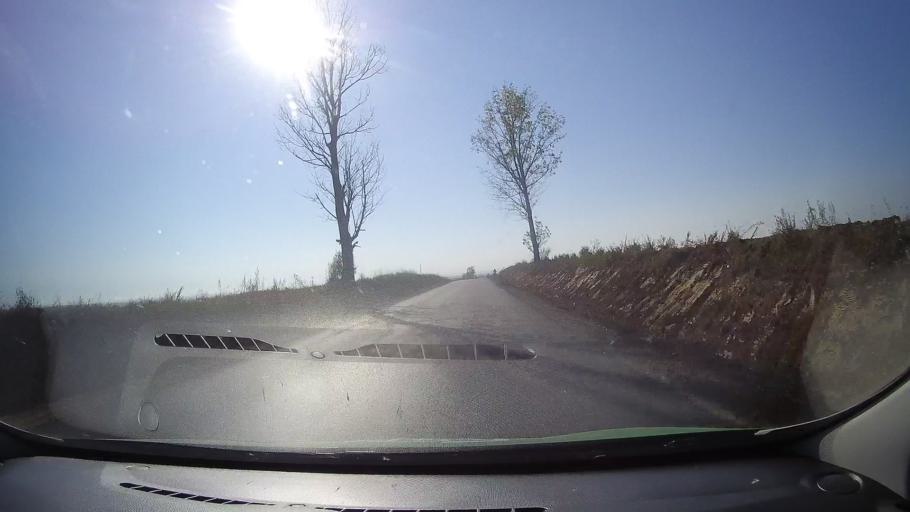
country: RO
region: Satu Mare
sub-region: Comuna Tiream
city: Tiream
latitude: 47.6456
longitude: 22.4637
